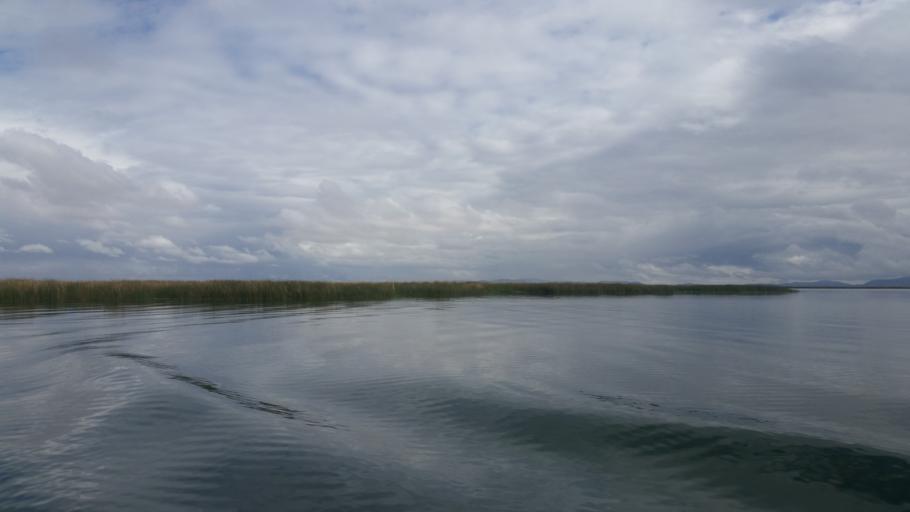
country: PE
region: Puno
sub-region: Provincia de Puno
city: Puno
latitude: -15.8486
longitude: -69.9633
